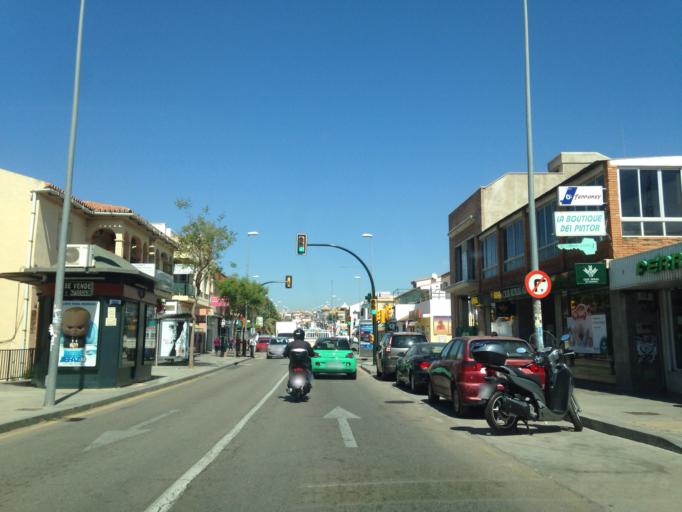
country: ES
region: Andalusia
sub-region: Provincia de Malaga
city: Malaga
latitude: 36.7370
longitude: -4.4798
